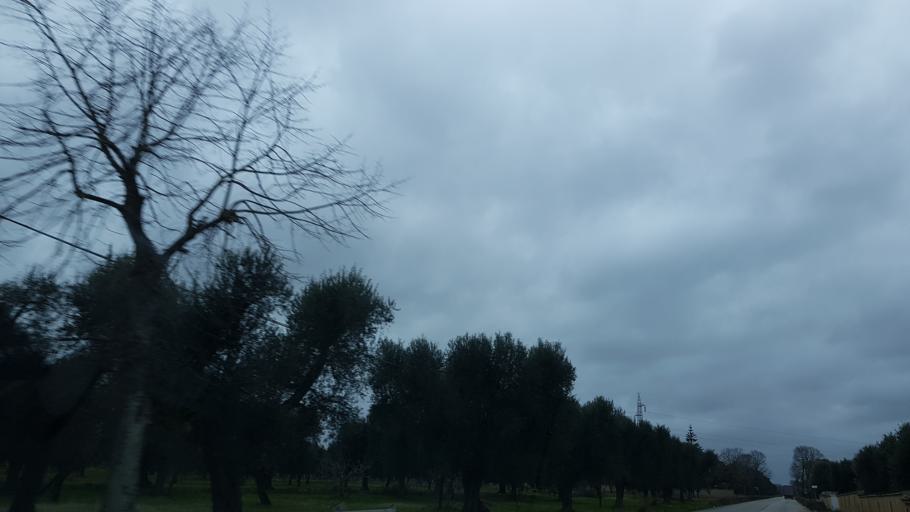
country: IT
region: Apulia
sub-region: Provincia di Brindisi
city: San Vito dei Normanni
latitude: 40.6552
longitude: 17.7577
